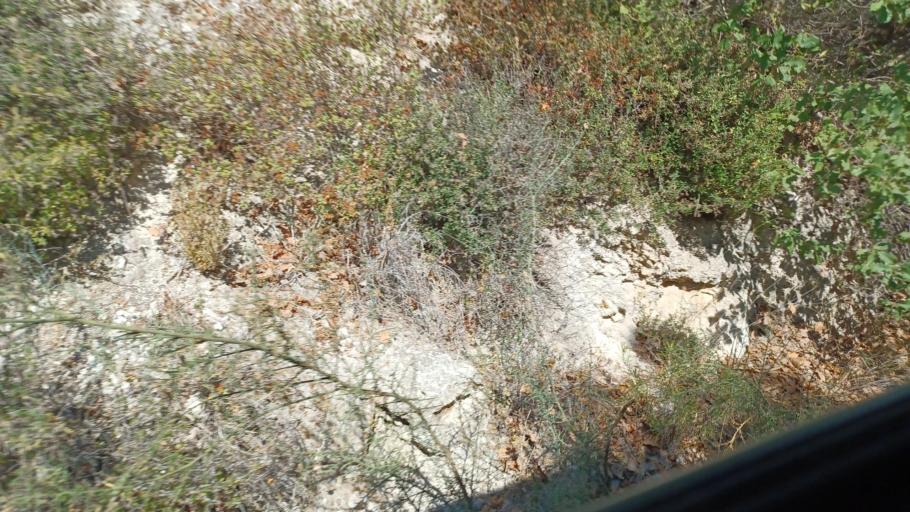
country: CY
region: Pafos
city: Tala
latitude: 34.9048
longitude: 32.4907
